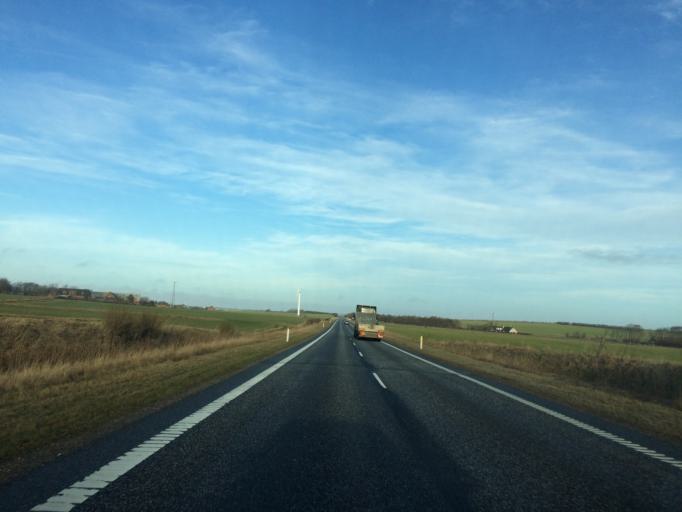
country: DK
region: North Denmark
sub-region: Thisted Kommune
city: Hurup
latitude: 56.7644
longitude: 8.4557
